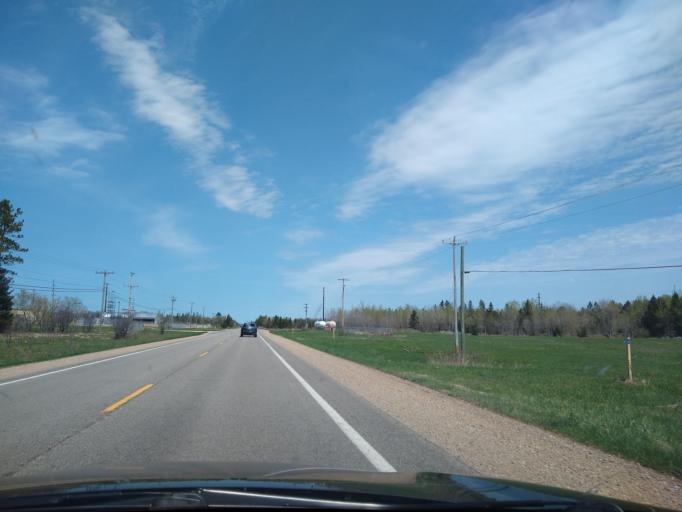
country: US
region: Michigan
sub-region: Delta County
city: Gladstone
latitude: 45.9418
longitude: -86.9720
